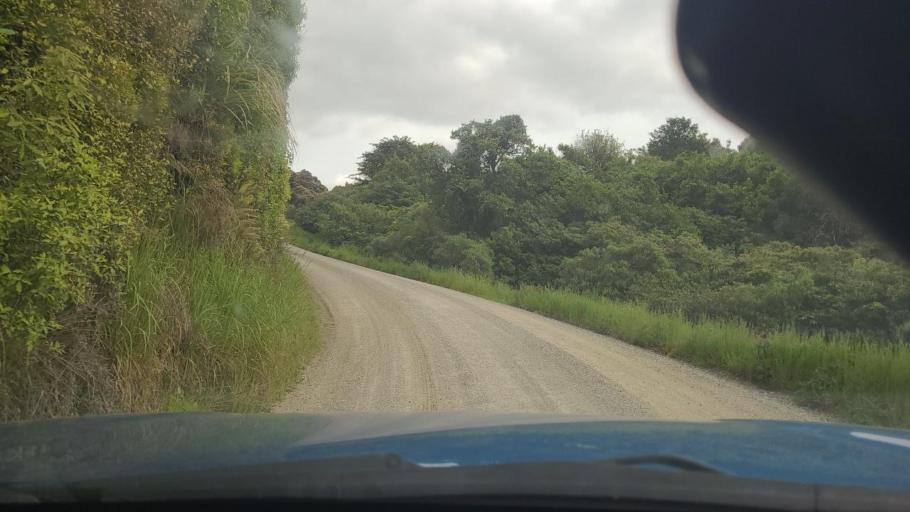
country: NZ
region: Otago
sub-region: Clutha District
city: Papatowai
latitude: -46.4961
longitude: 169.1618
